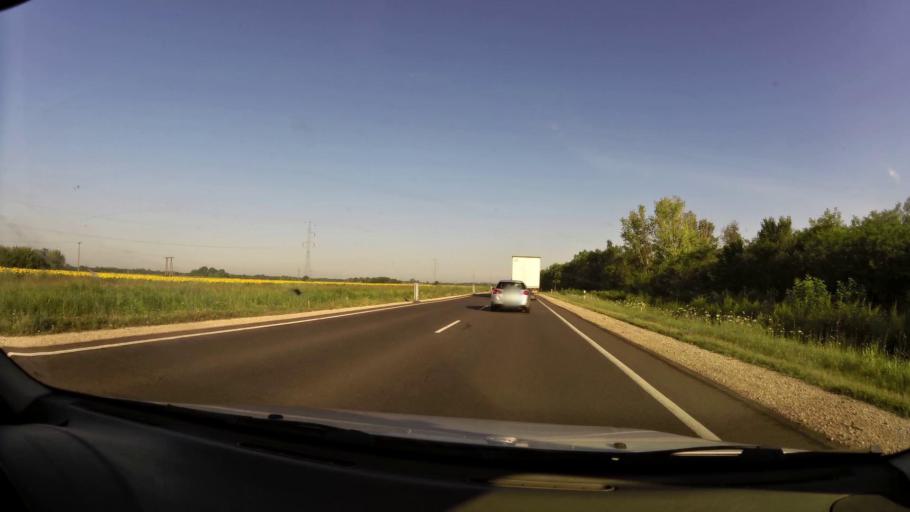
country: HU
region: Pest
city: Cegled
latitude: 47.2085
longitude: 19.7583
